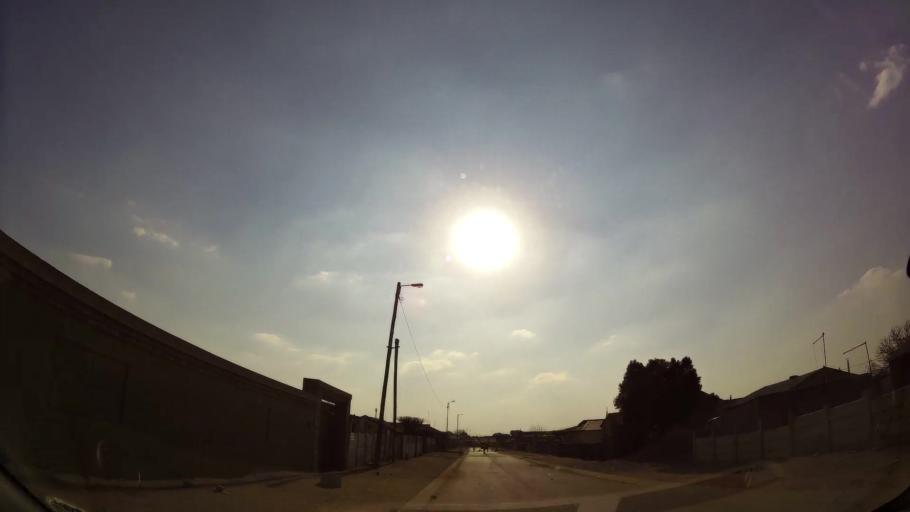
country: ZA
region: Gauteng
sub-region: Ekurhuleni Metropolitan Municipality
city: Brakpan
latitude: -26.1462
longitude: 28.4183
